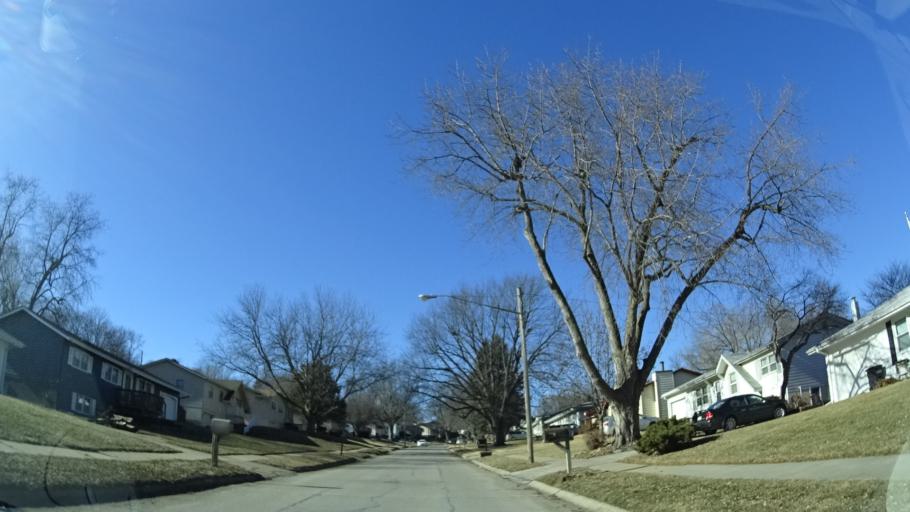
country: US
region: Nebraska
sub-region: Sarpy County
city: Offutt Air Force Base
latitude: 41.1470
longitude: -95.9206
